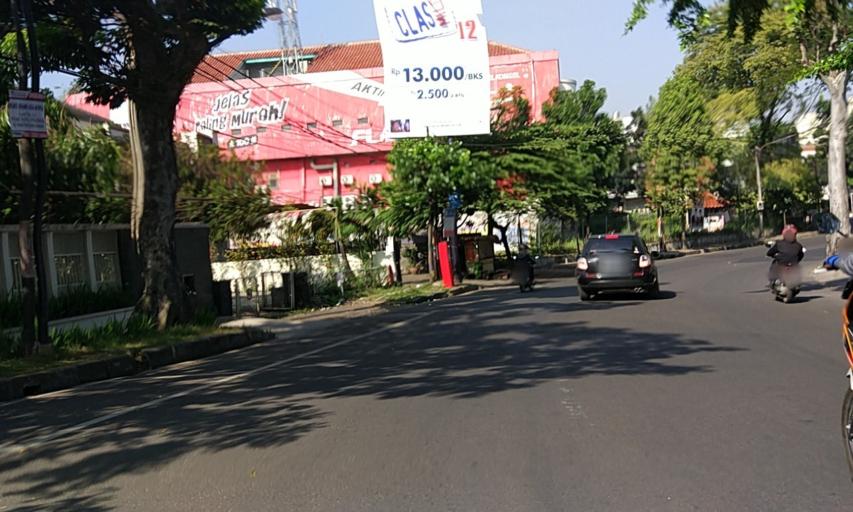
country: ID
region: West Java
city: Bandung
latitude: -6.9174
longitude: 107.6135
